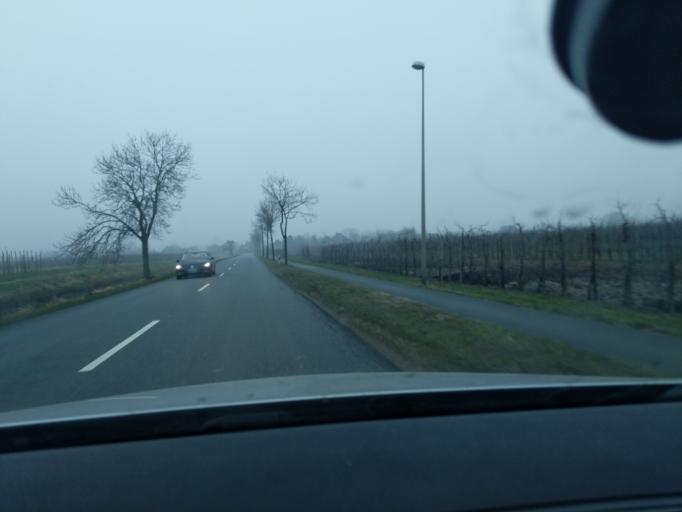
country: DE
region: Lower Saxony
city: Jork
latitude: 53.5464
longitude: 9.6617
